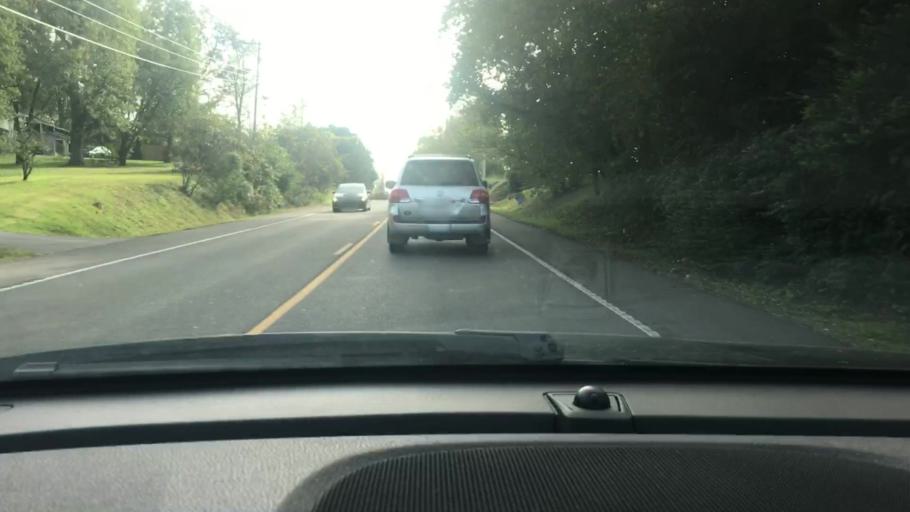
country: US
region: Tennessee
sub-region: Williamson County
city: Franklin
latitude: 35.9415
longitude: -86.8560
